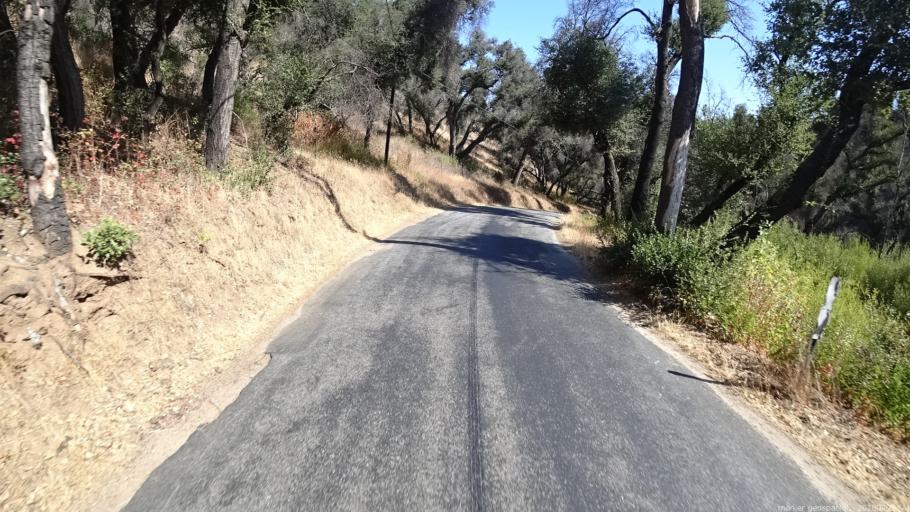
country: US
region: California
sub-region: Monterey County
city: Gonzales
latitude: 36.3871
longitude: -121.5962
